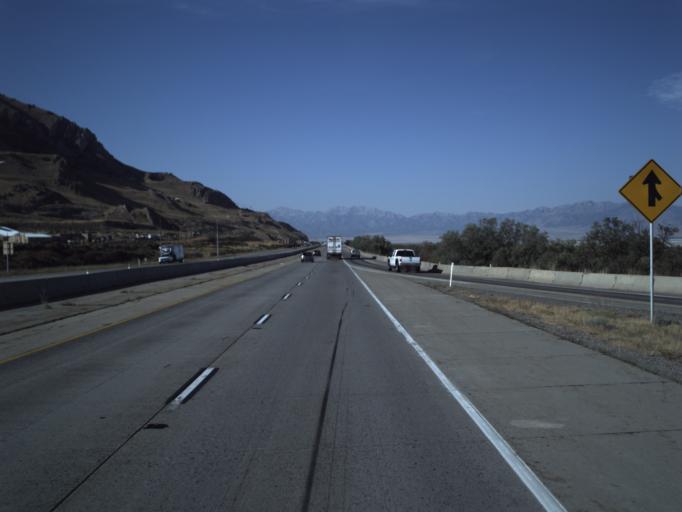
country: US
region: Utah
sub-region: Tooele County
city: Stansbury park
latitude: 40.7215
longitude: -112.2292
